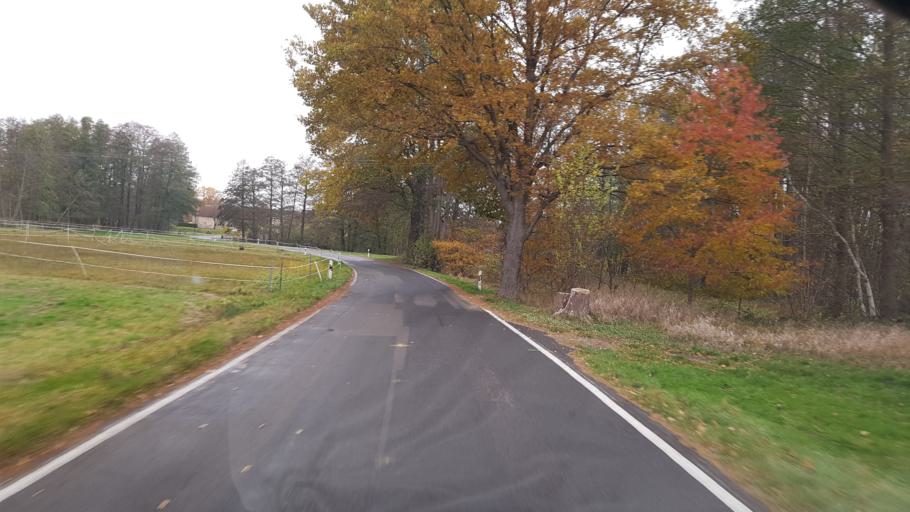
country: DE
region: Brandenburg
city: Ortrand
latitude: 51.3628
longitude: 13.7630
